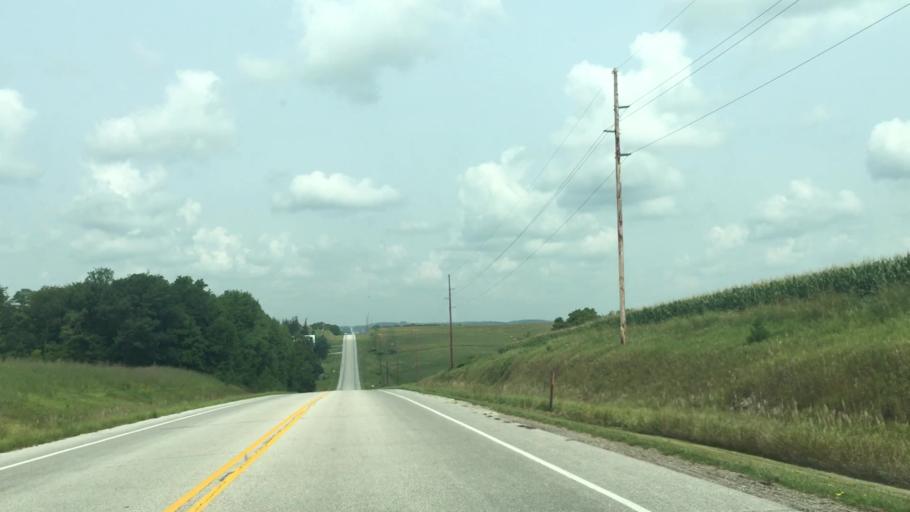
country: US
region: Minnesota
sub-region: Fillmore County
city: Harmony
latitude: 43.5716
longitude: -91.9298
